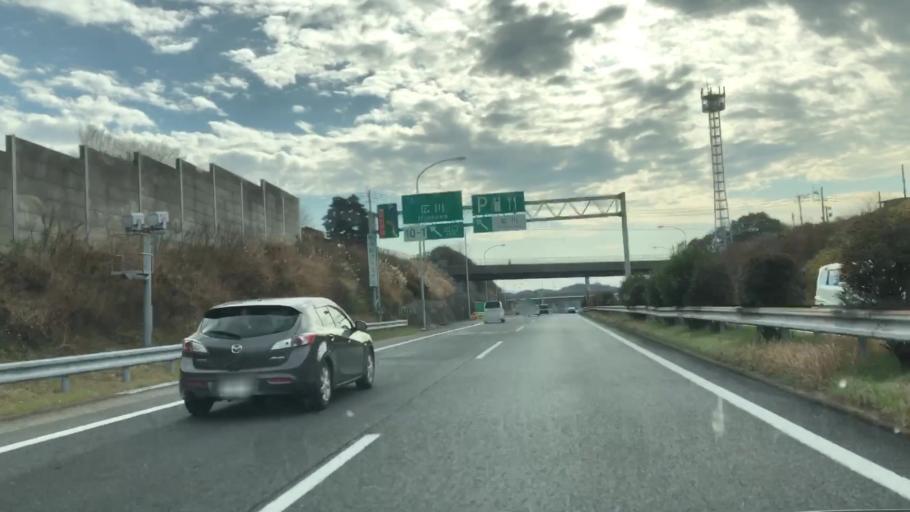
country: JP
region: Fukuoka
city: Kurume
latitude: 33.2585
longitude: 130.5378
